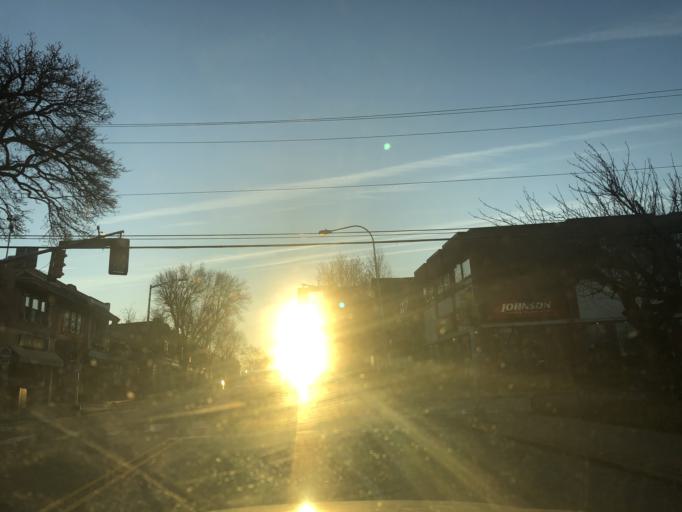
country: US
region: Pennsylvania
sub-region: Montgomery County
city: Bryn Mawr
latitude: 40.0225
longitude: -75.3204
